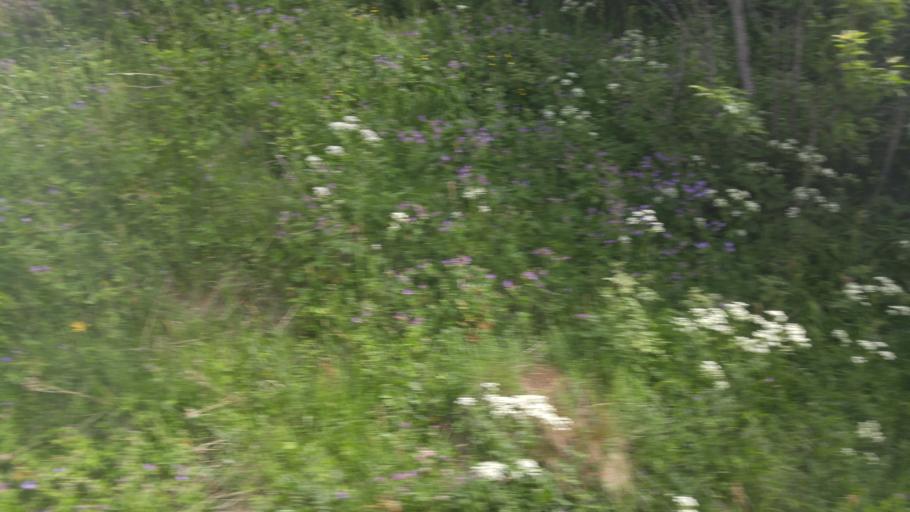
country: NO
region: Sor-Trondelag
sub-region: Midtre Gauldal
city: Storen
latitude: 62.9963
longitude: 10.4710
